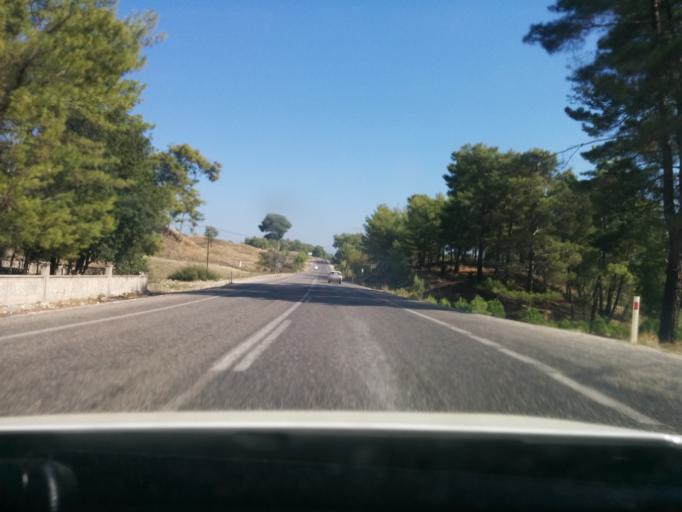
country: TR
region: Mugla
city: Esen
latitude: 36.4857
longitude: 29.3157
